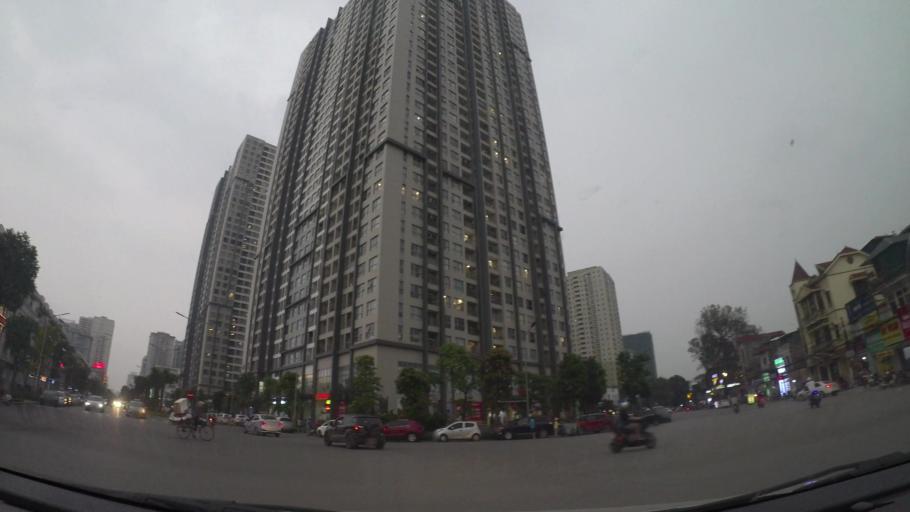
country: VN
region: Ha Noi
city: Cau Dien
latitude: 21.0366
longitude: 105.7596
